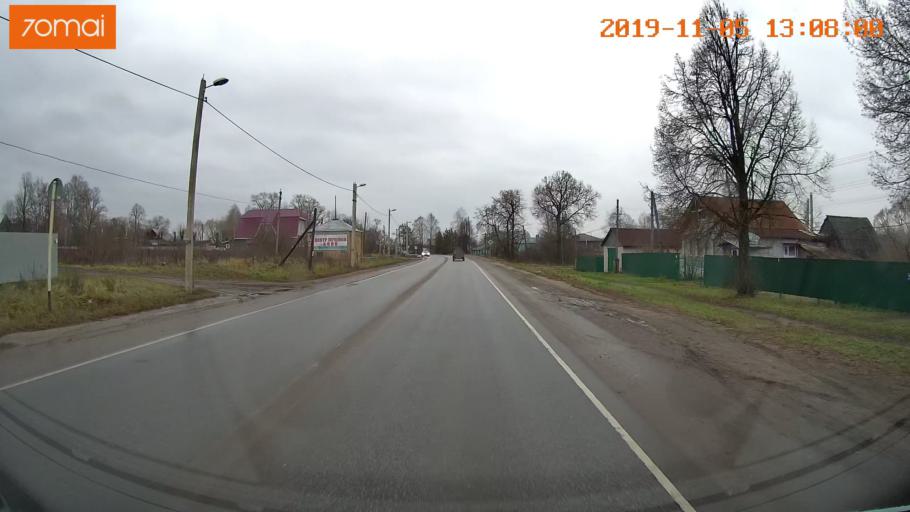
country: RU
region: Ivanovo
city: Kitovo
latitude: 56.8653
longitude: 41.2870
